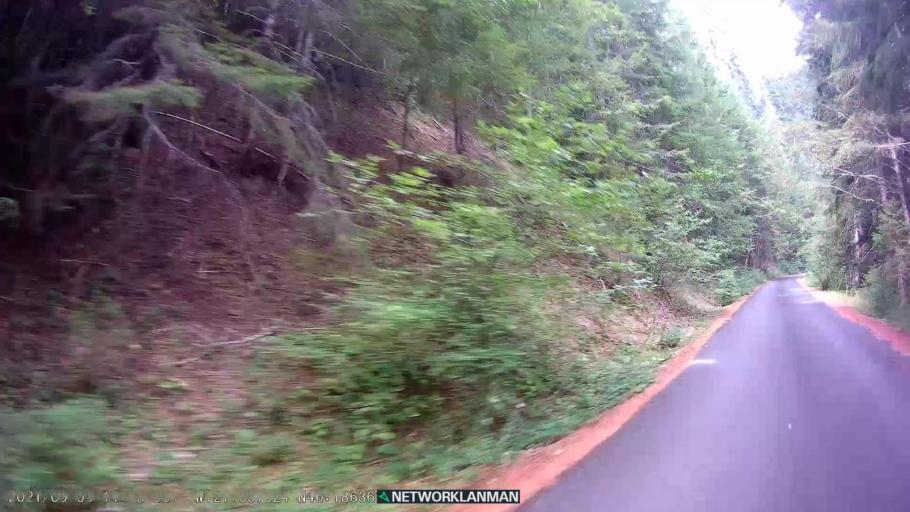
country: US
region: Washington
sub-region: Skamania County
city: Carson
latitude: 46.1866
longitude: -121.8574
